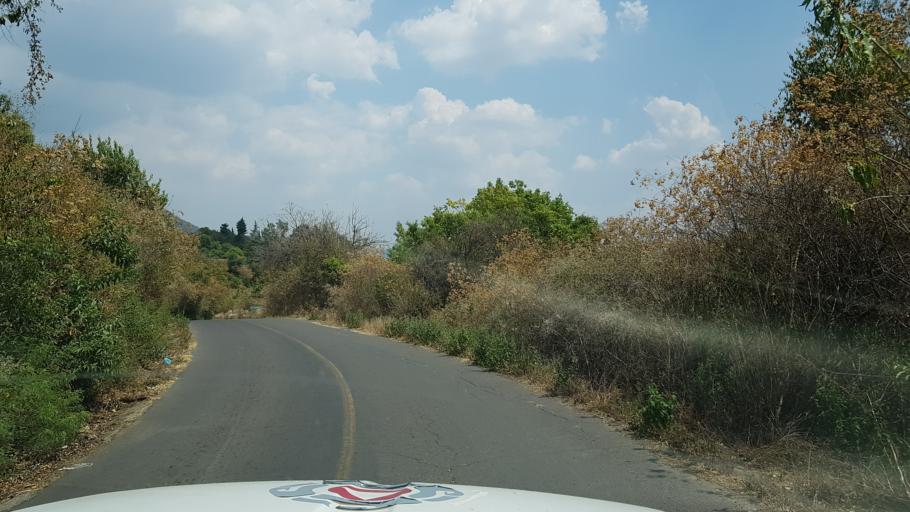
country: MX
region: Morelos
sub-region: Yecapixtla
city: Texcala
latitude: 18.9199
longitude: -98.8118
